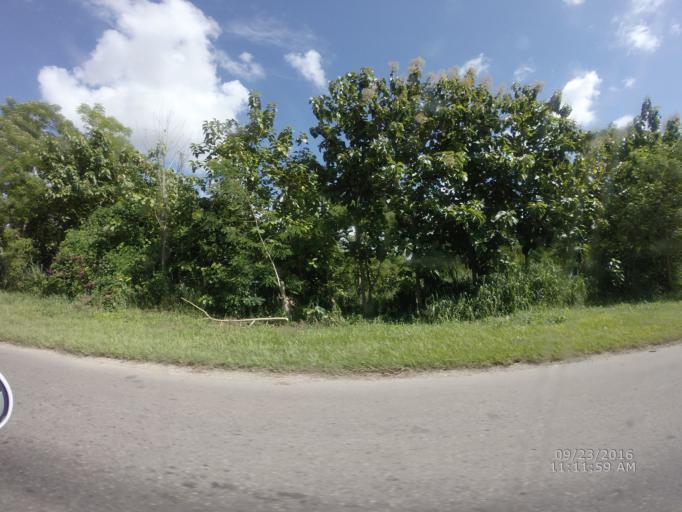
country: CU
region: La Habana
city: Arroyo Naranjo
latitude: 23.0275
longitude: -82.2769
